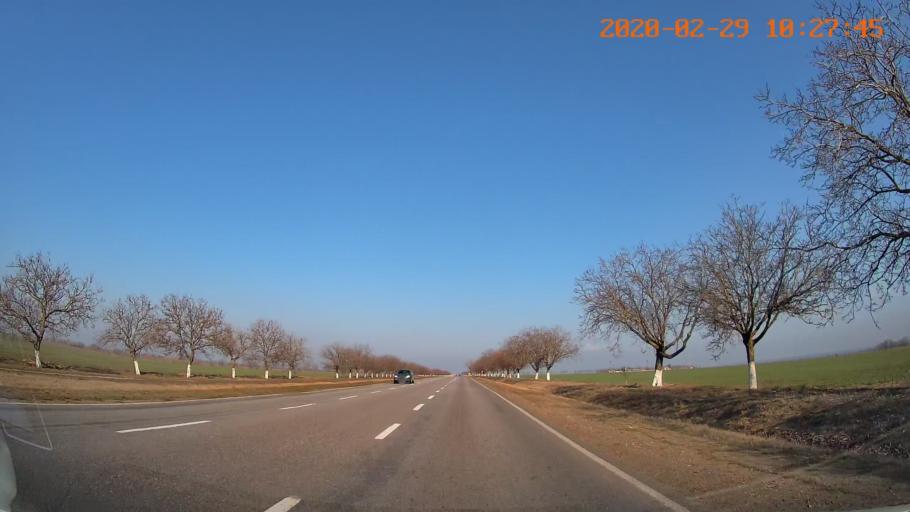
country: MD
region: Telenesti
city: Tiraspolul Nou
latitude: 46.9005
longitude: 29.5958
